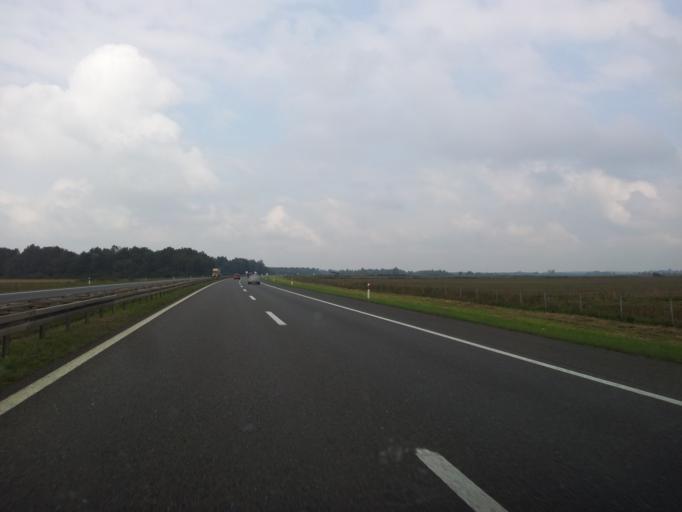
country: HR
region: Sisacko-Moslavacka
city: Osekovo
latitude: 45.5767
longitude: 16.5665
